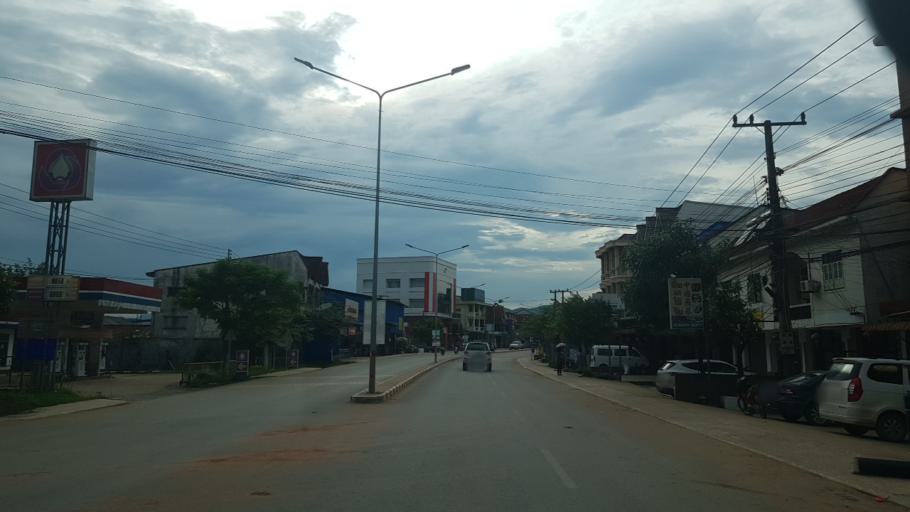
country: LA
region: Oudomxai
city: Muang Xay
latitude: 20.6885
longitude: 101.9860
